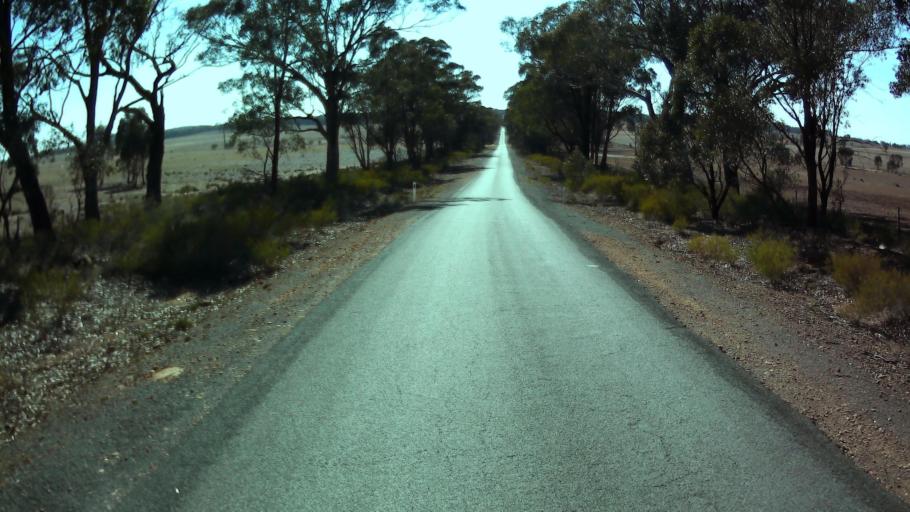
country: AU
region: New South Wales
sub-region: Weddin
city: Grenfell
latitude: -33.7822
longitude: 147.9637
